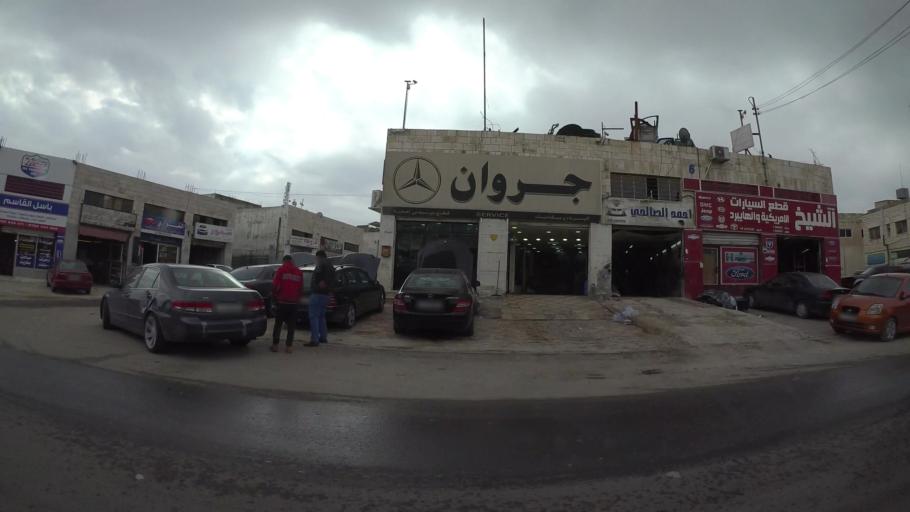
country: JO
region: Amman
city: Wadi as Sir
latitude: 31.9456
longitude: 35.8371
